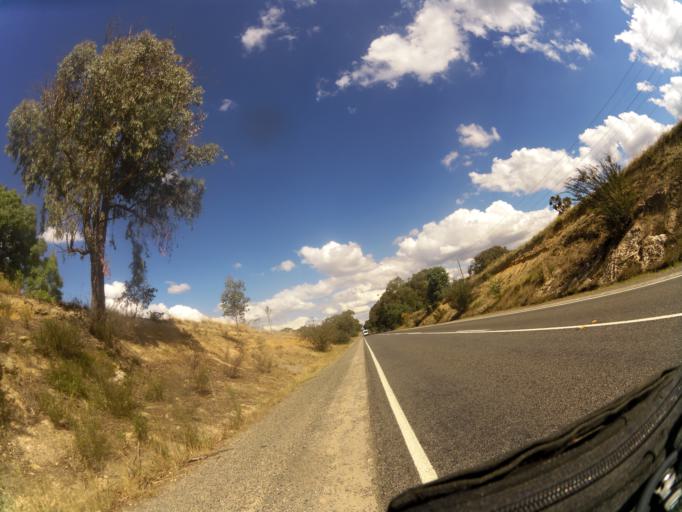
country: AU
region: Victoria
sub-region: Mansfield
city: Mansfield
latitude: -36.8814
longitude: 145.9942
